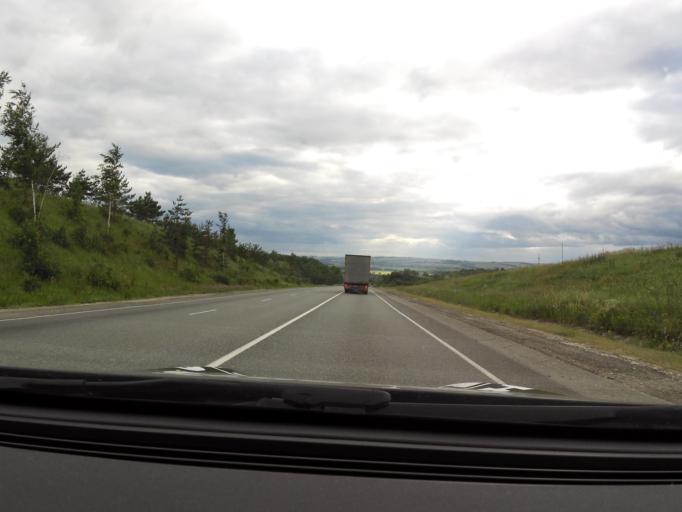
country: RU
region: Tatarstan
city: Sviyazhsk
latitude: 55.7197
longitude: 48.7381
